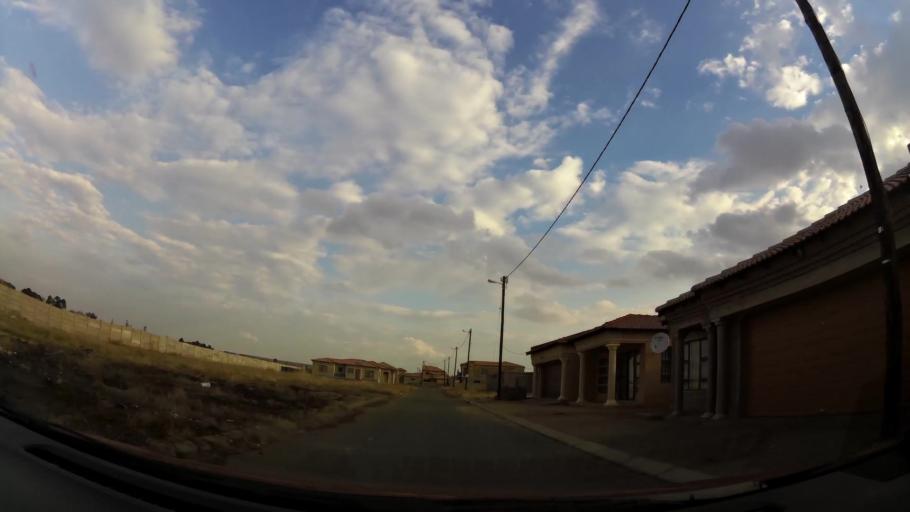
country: ZA
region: Gauteng
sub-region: Sedibeng District Municipality
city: Vanderbijlpark
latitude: -26.6095
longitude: 27.8150
